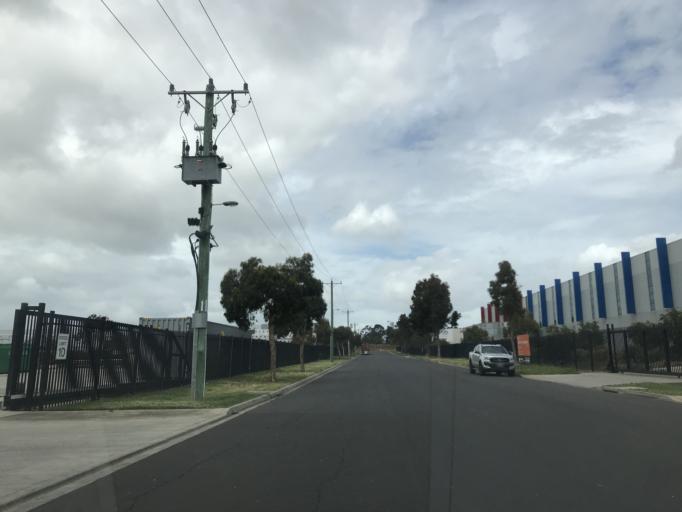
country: AU
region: Victoria
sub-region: Brimbank
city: Derrimut
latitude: -37.7888
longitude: 144.7752
